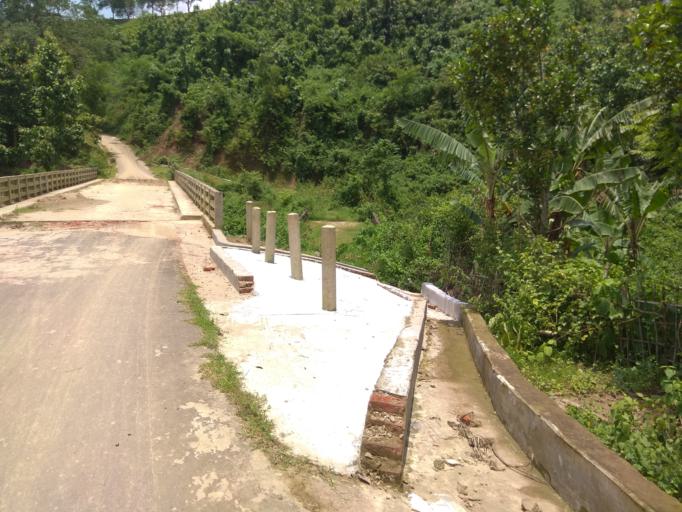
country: BD
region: Chittagong
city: Manikchari
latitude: 22.8944
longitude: 91.9228
